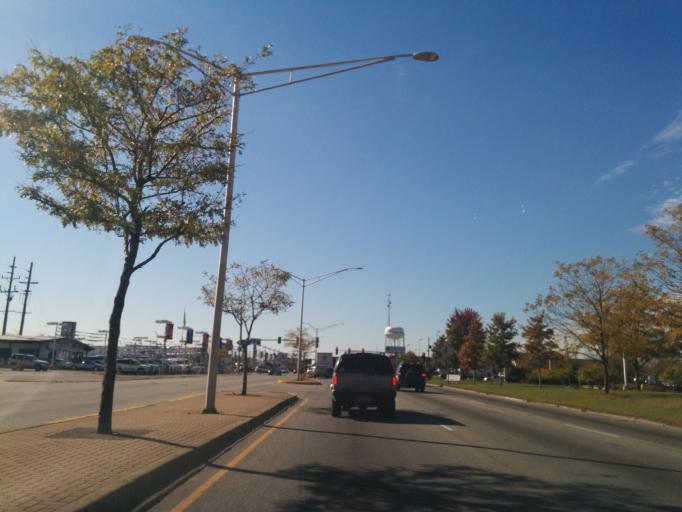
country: US
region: Illinois
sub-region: Cook County
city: Melrose Park
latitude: 41.9079
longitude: -87.8627
